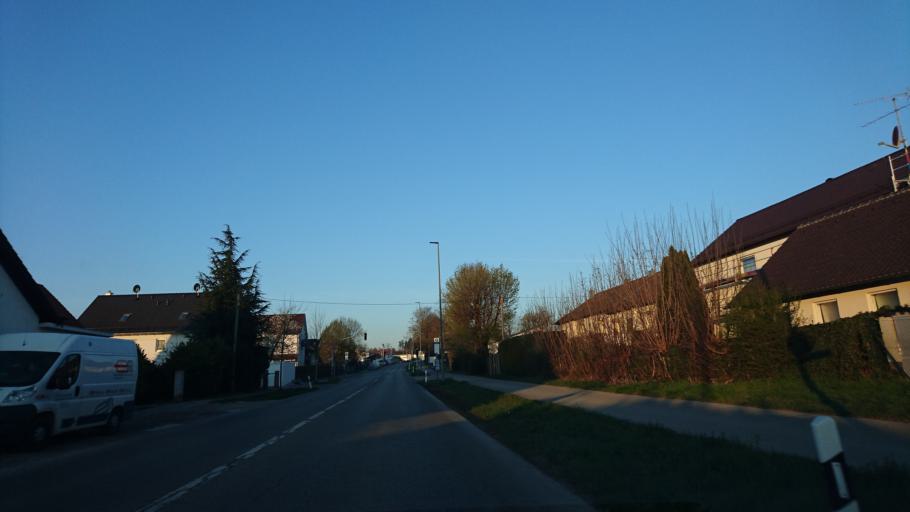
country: DE
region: Bavaria
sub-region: Swabia
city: Stadtbergen
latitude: 48.3740
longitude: 10.8218
